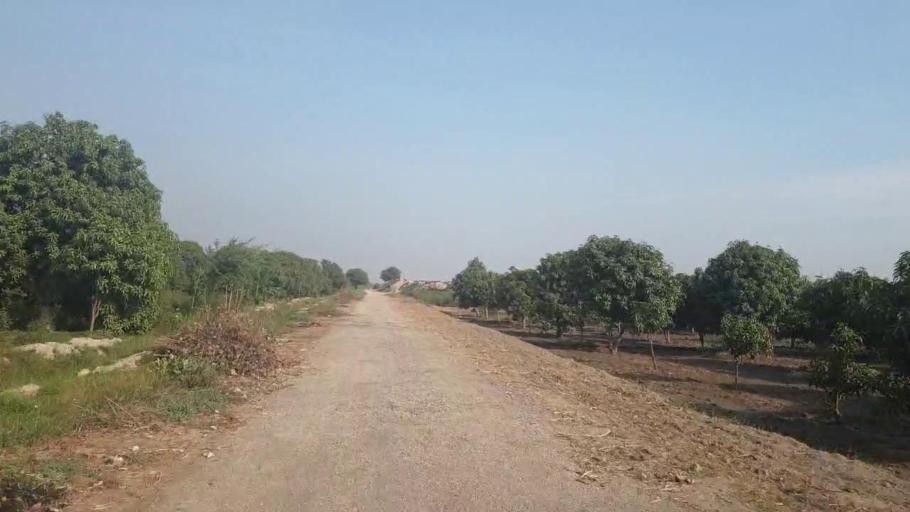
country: PK
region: Sindh
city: Tando Jam
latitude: 25.4295
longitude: 68.4693
